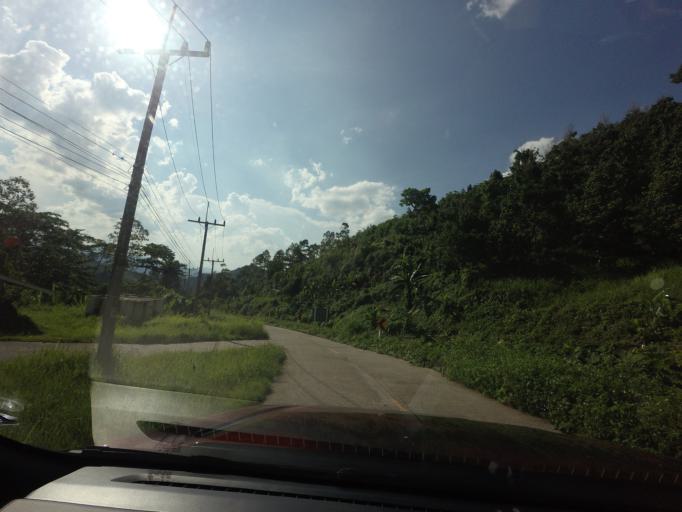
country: TH
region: Yala
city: Than To
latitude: 6.0889
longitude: 101.3213
